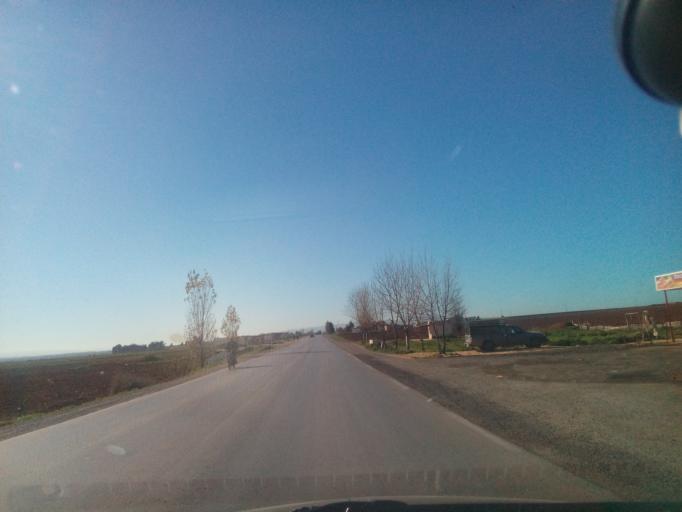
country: DZ
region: Relizane
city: Djidiouia
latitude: 35.8968
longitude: 0.6754
